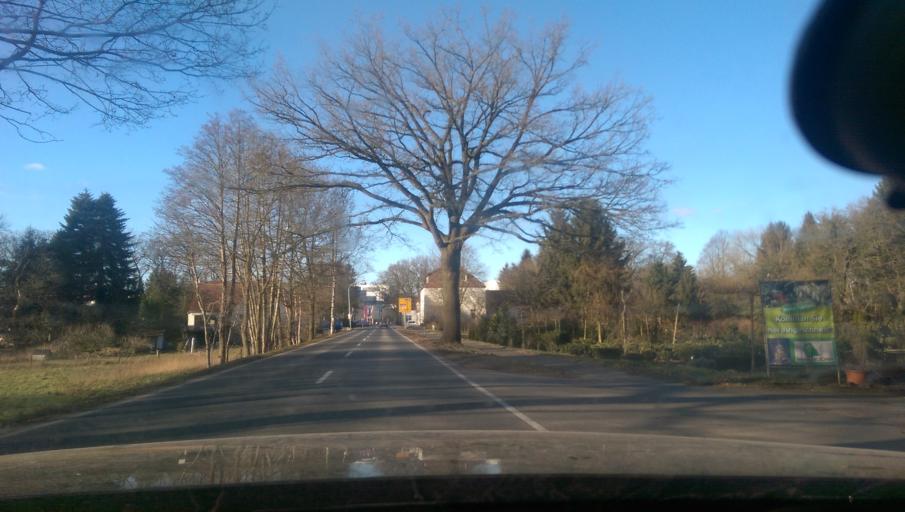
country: DE
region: Lower Saxony
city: Hellwege
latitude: 53.0544
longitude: 9.1736
